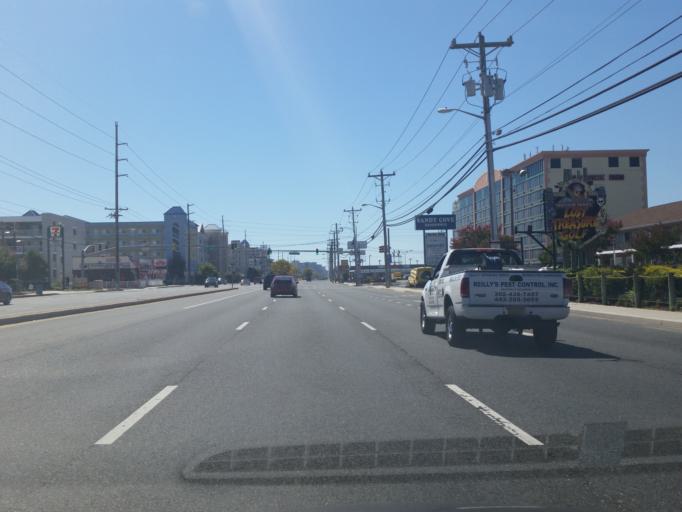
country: US
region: Delaware
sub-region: Sussex County
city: Bethany Beach
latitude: 38.4453
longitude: -75.0530
